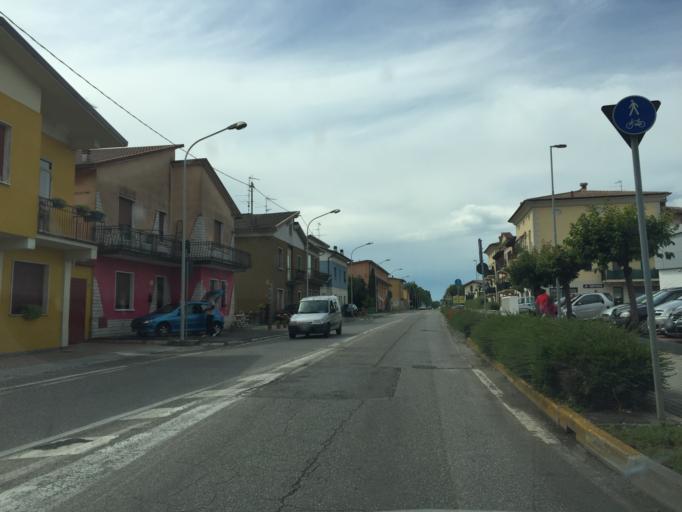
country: IT
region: Lombardy
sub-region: Provincia di Brescia
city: Ghedi
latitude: 45.4087
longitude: 10.2756
